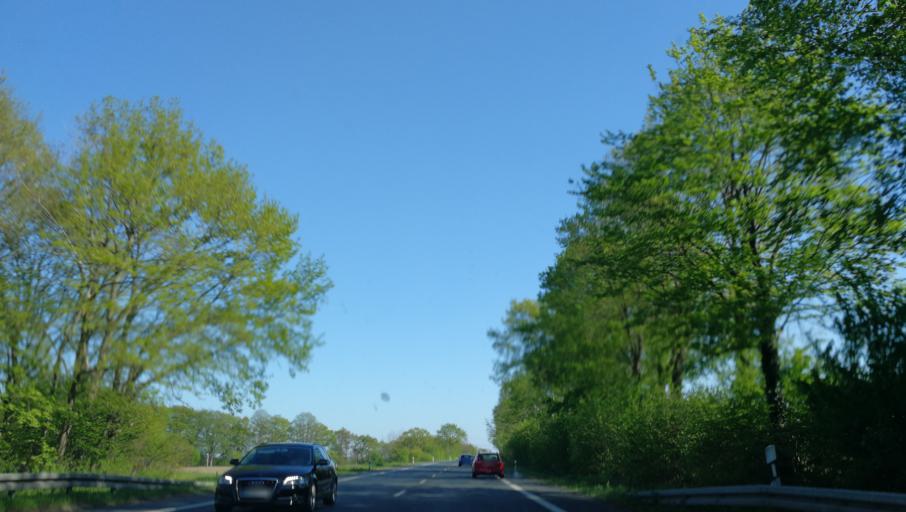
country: DE
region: North Rhine-Westphalia
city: Emsdetten
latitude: 52.1876
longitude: 7.5278
